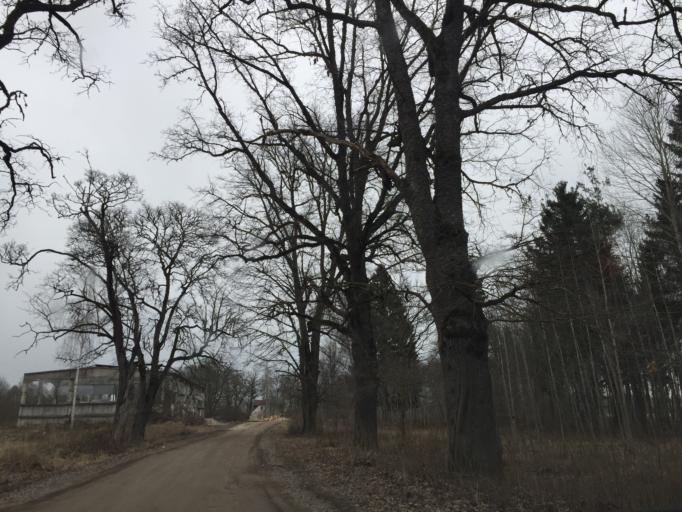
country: LV
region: Plavinu
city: Plavinas
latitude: 56.6025
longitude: 25.6595
